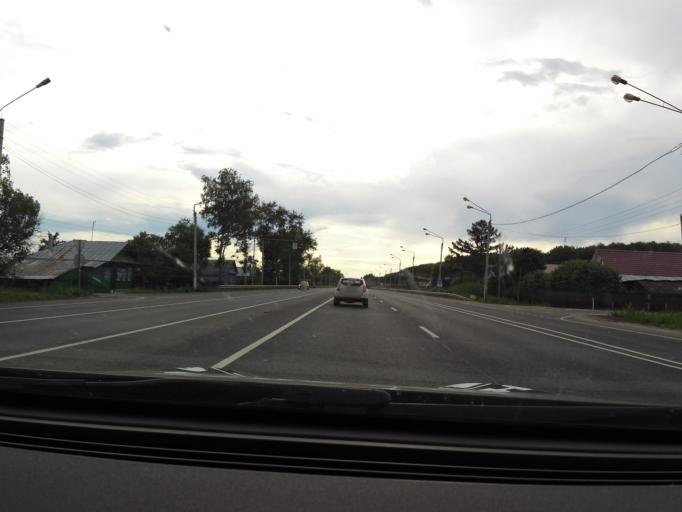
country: RU
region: Vladimir
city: Luknovo
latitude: 56.2390
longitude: 42.0595
